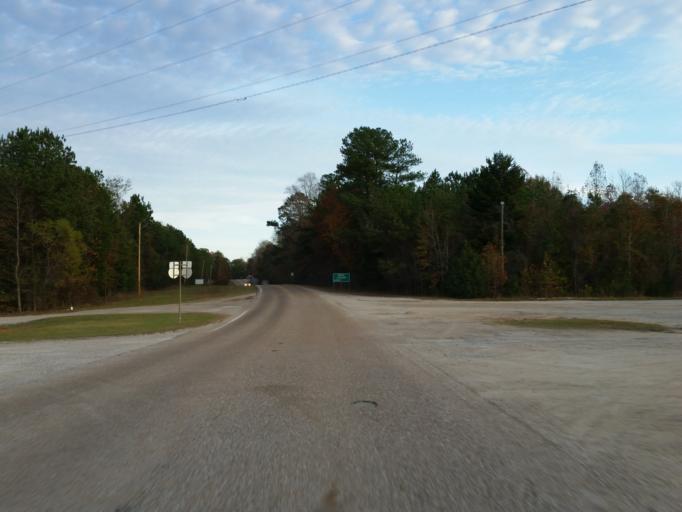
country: US
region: Alabama
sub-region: Sumter County
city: York
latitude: 32.4252
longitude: -88.4479
